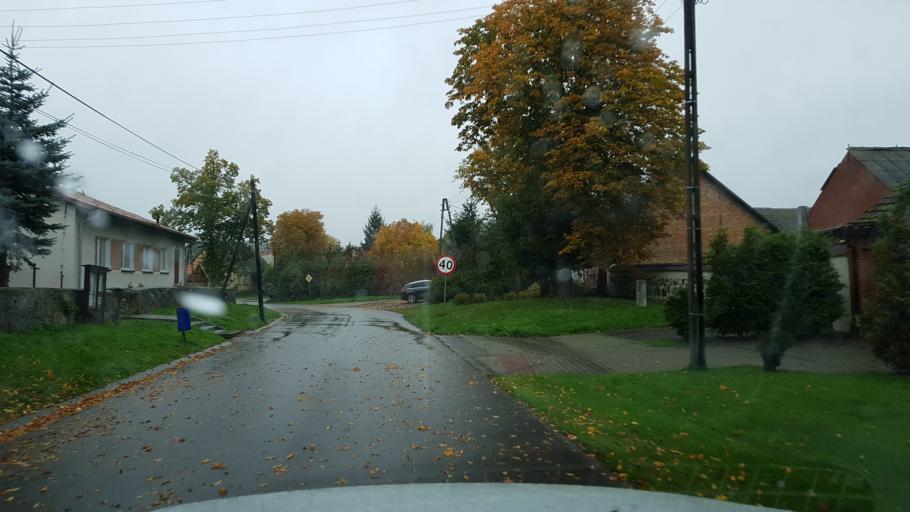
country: PL
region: West Pomeranian Voivodeship
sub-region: Powiat pyrzycki
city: Bielice
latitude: 53.1999
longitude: 14.8021
